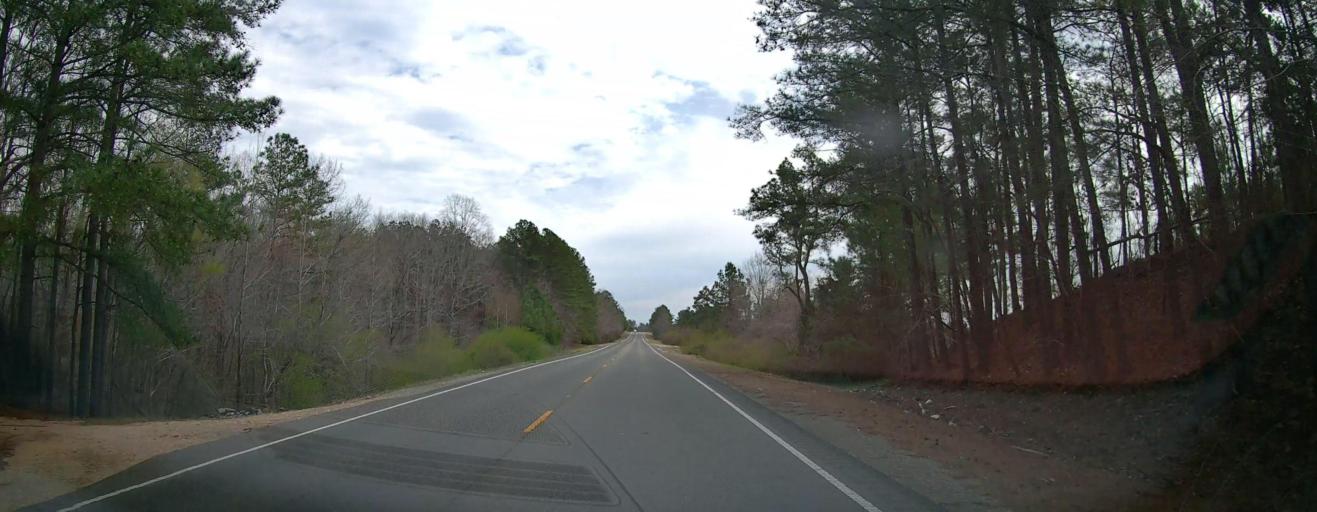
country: US
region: Alabama
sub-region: Marion County
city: Guin
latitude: 34.0435
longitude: -87.9570
